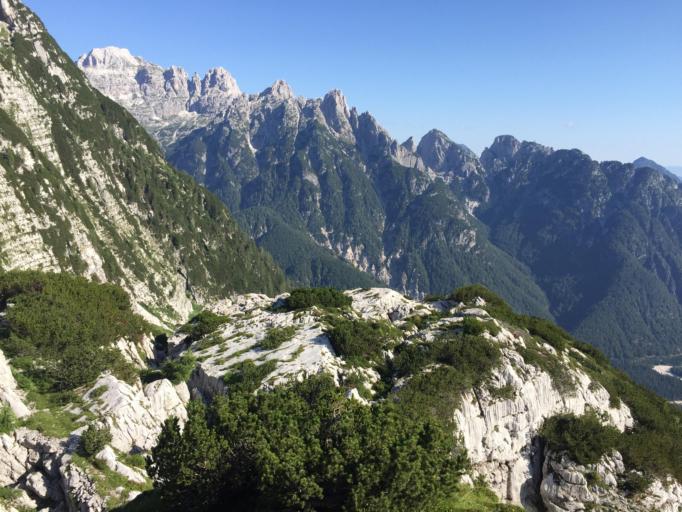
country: SI
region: Bovec
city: Bovec
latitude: 46.3869
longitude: 13.5305
